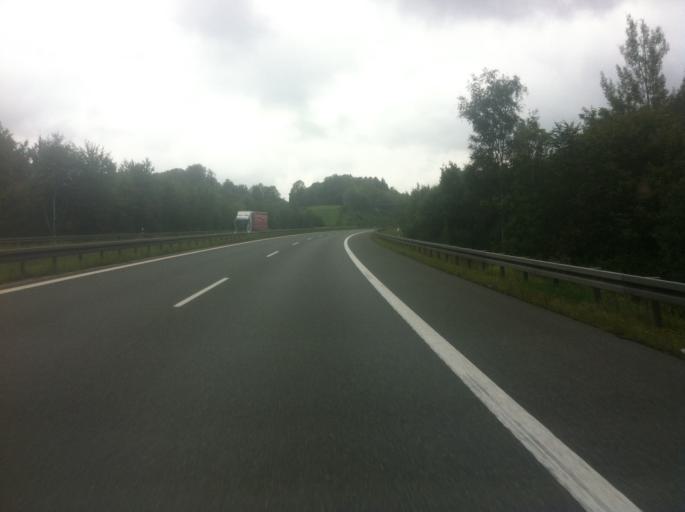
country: DE
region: Bavaria
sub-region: Upper Palatinate
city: Ursensollen
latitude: 49.3977
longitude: 11.7929
